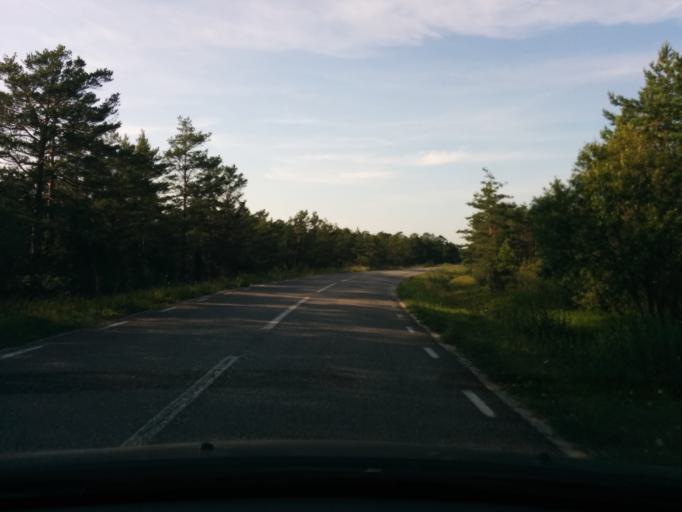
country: SE
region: Gotland
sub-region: Gotland
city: Slite
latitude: 57.5356
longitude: 18.6990
